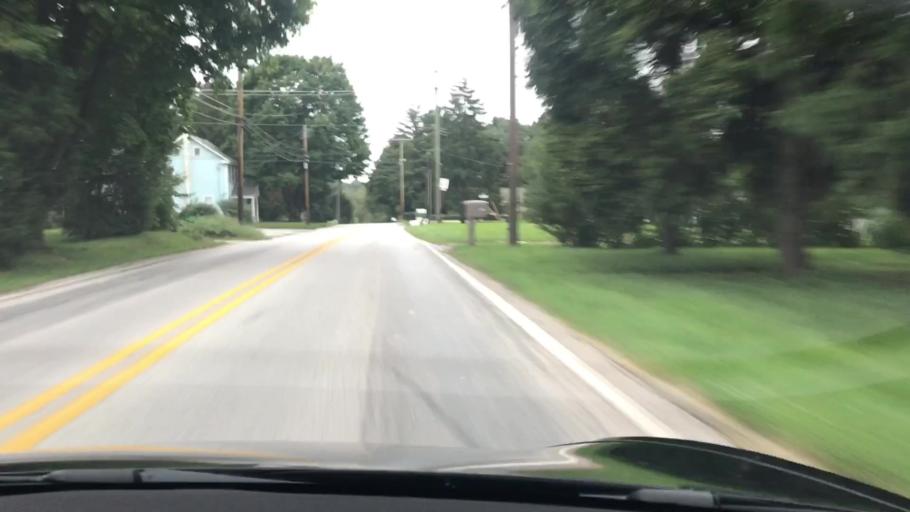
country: US
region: Pennsylvania
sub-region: York County
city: Dover
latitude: 40.0060
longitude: -76.8343
